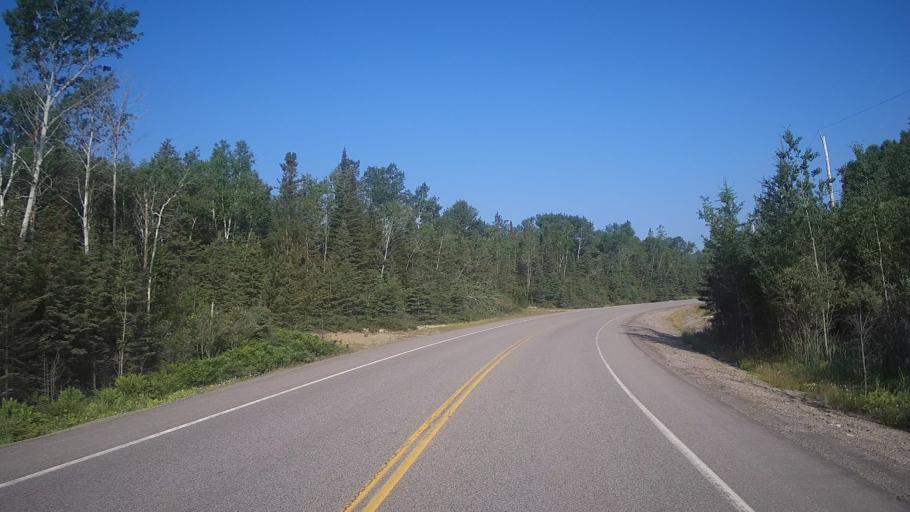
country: CA
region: Ontario
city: Rayside-Balfour
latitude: 46.7314
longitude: -81.5875
